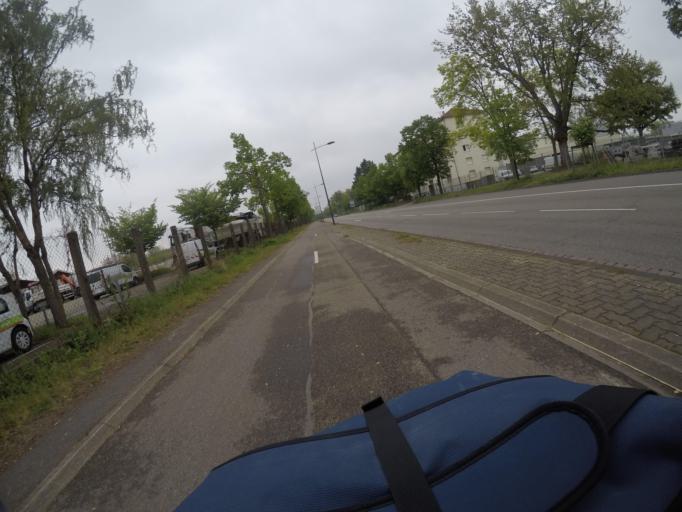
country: FR
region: Alsace
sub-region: Departement du Bas-Rhin
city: Strasbourg
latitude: 48.5659
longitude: 7.7388
